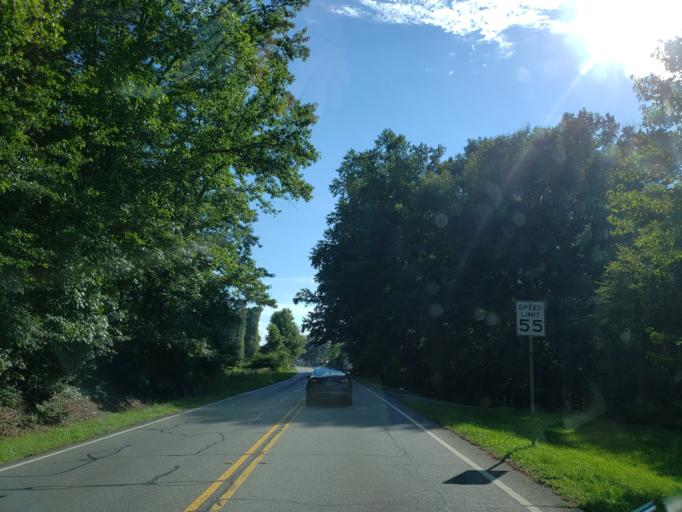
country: US
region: Georgia
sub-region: Fulton County
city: Milton
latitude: 34.2361
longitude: -84.2620
